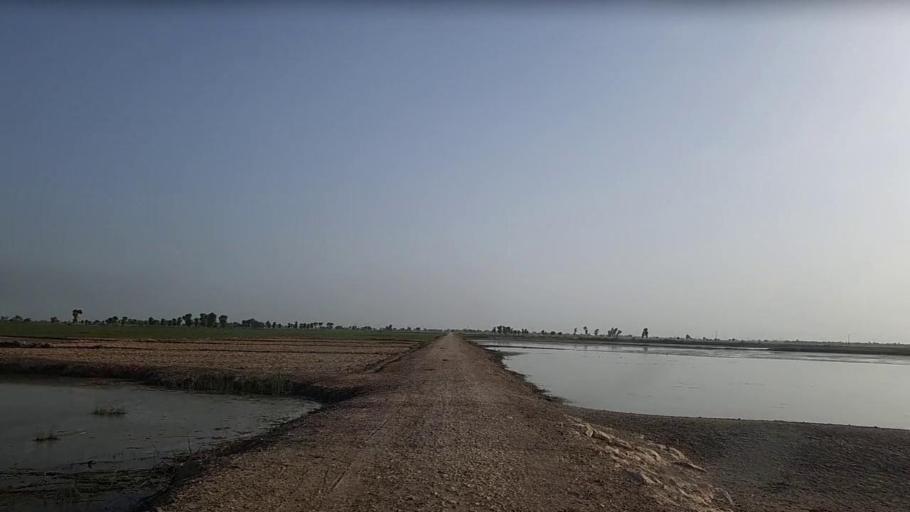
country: PK
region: Sindh
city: Sita Road
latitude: 27.1058
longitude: 67.8892
